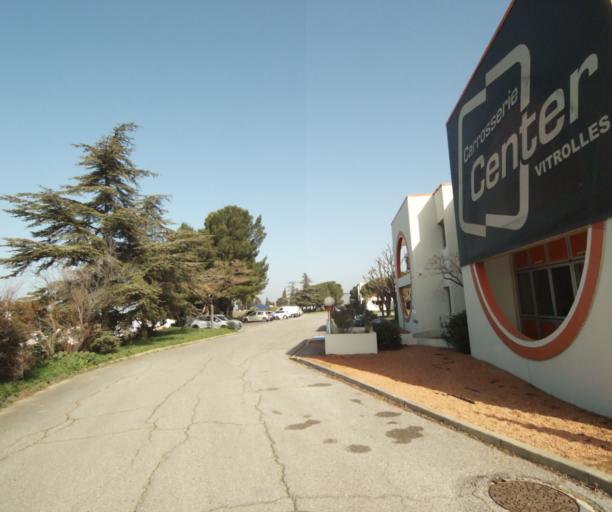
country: FR
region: Provence-Alpes-Cote d'Azur
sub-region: Departement des Bouches-du-Rhone
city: Saint-Victoret
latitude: 43.4422
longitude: 5.2332
